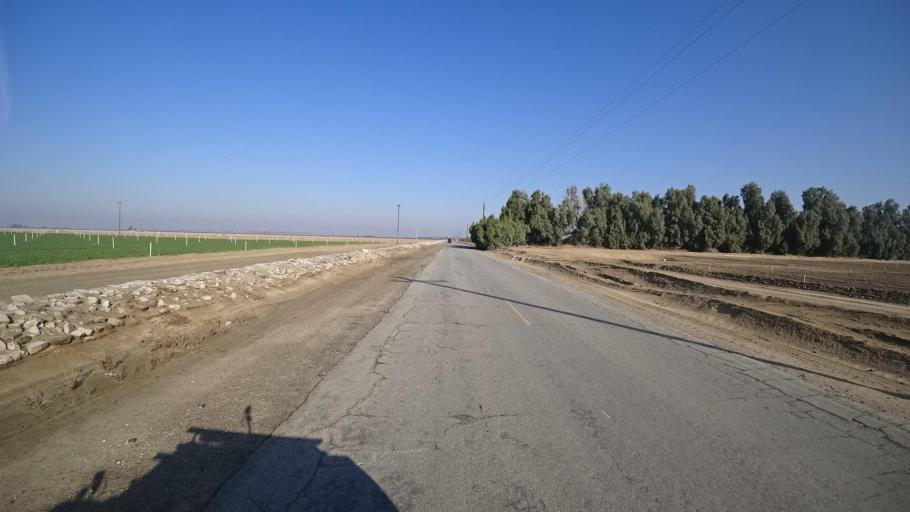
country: US
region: California
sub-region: Kern County
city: Weedpatch
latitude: 35.1285
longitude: -118.9678
